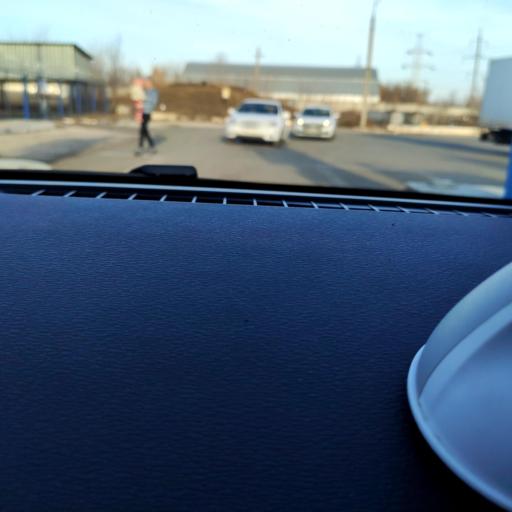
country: RU
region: Samara
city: Petra-Dubrava
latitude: 53.2602
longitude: 50.2846
